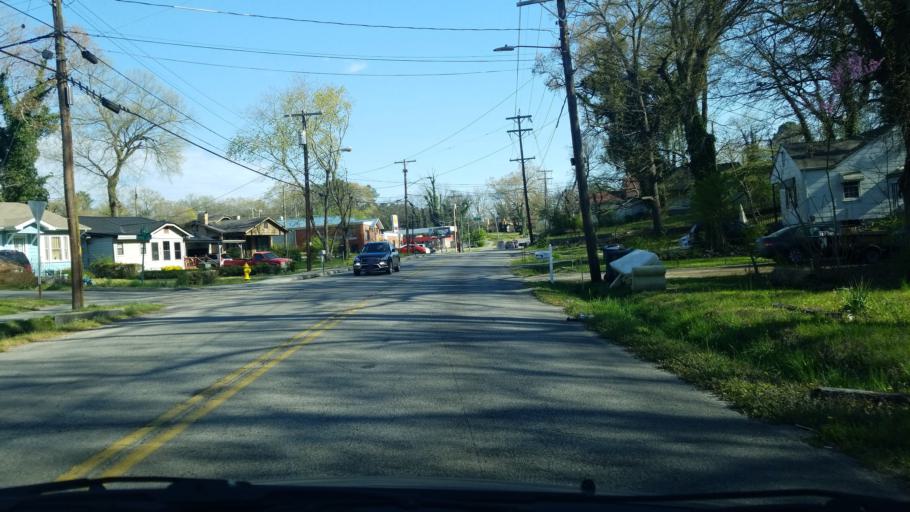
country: US
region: Tennessee
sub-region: Hamilton County
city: East Chattanooga
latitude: 35.0456
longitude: -85.2377
